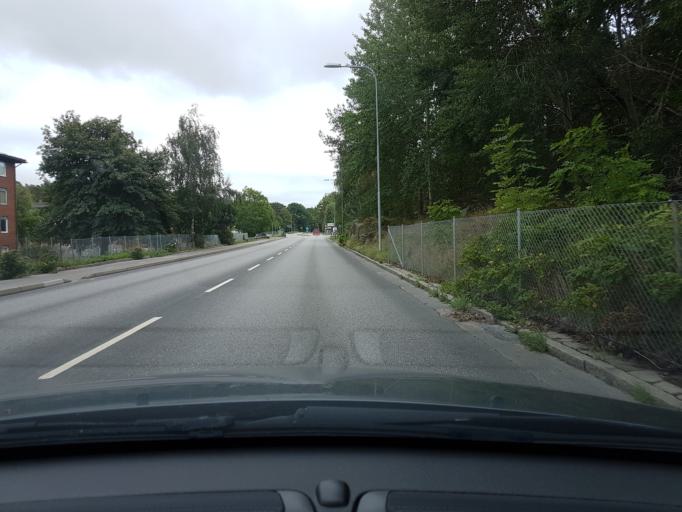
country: SE
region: Vaestra Goetaland
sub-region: Goteborg
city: Majorna
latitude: 57.6414
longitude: 11.8961
